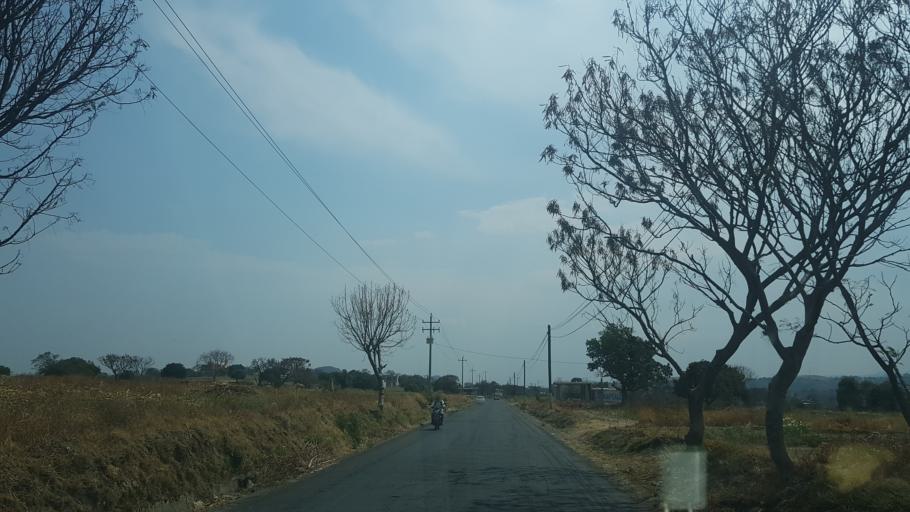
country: MX
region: Puebla
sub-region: Tianguismanalco
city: San Martin Tlapala
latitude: 18.9716
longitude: -98.4542
